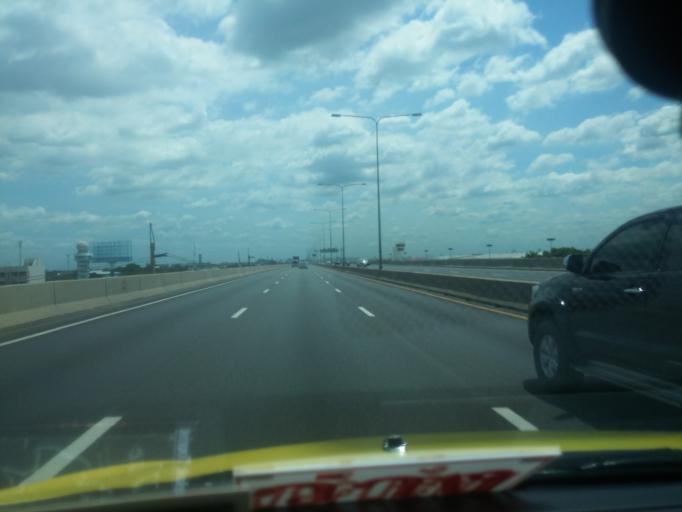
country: TH
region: Bangkok
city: Don Mueang
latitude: 13.9049
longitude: 100.5929
